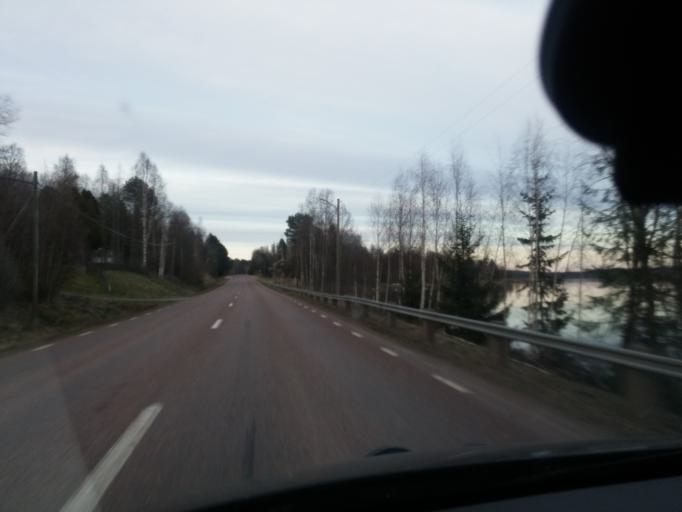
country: SE
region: Dalarna
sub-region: Faluns Kommun
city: Bjursas
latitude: 60.7143
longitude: 15.3214
